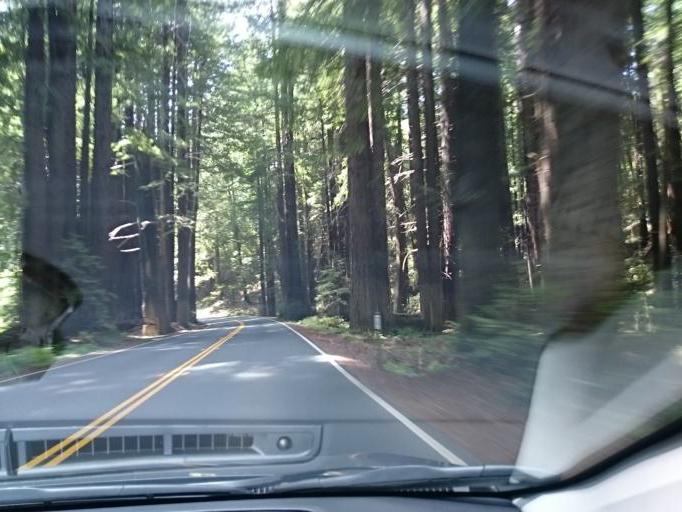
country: US
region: California
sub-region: Mendocino County
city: Boonville
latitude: 39.1559
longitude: -123.6238
